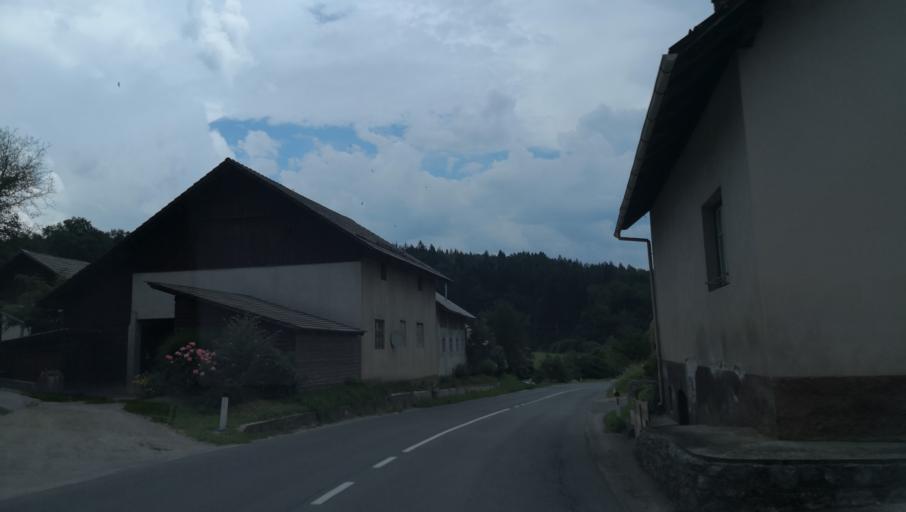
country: SI
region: Ivancna Gorica
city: Ivancna Gorica
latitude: 45.8812
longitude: 14.7970
